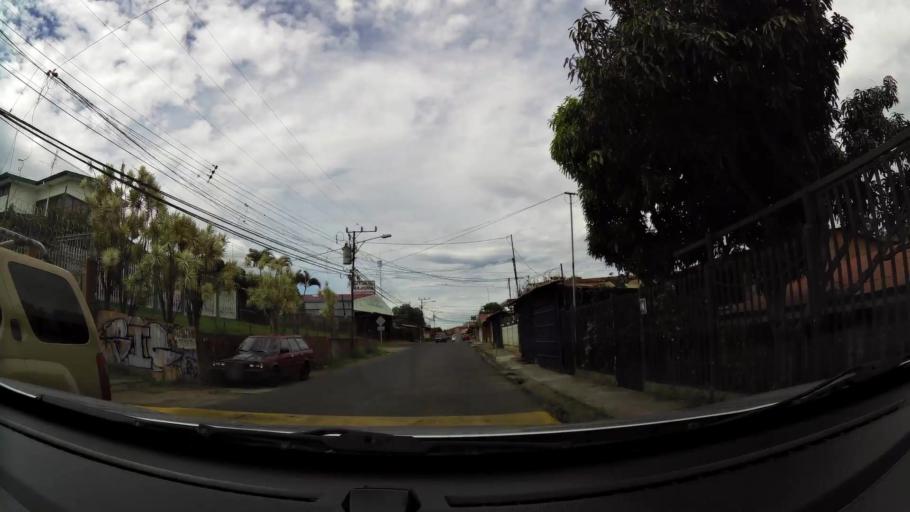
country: CR
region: San Jose
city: San Rafael Arriba
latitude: 9.8868
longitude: -84.0690
